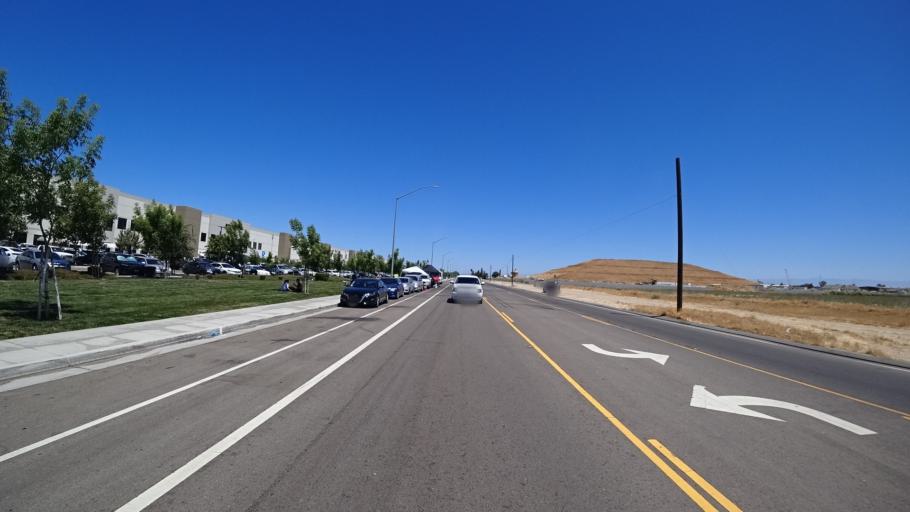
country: US
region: California
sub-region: Fresno County
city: Easton
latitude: 36.6820
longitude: -119.7637
